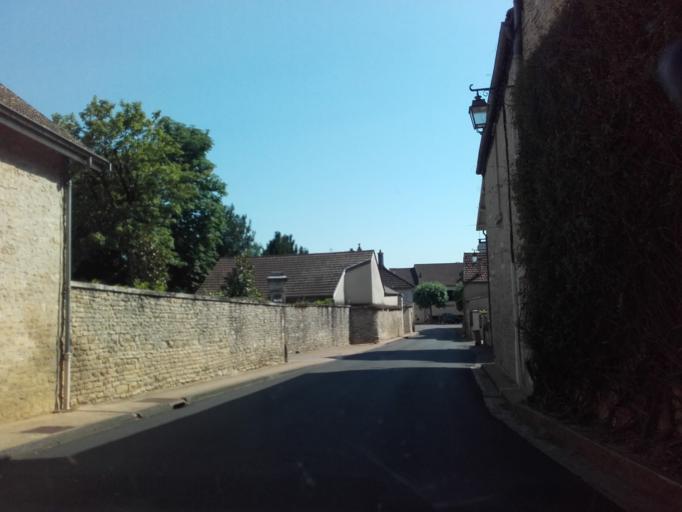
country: FR
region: Bourgogne
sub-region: Departement de la Cote-d'Or
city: Meursault
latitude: 46.9833
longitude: 4.7684
